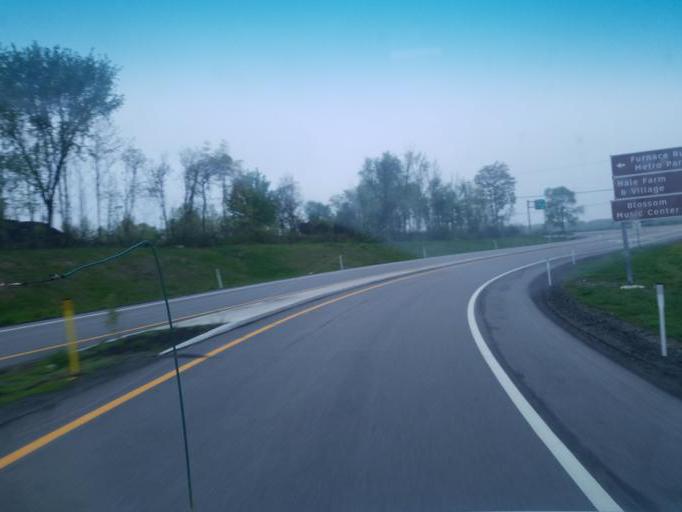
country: US
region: Ohio
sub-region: Summit County
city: Peninsula
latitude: 41.2444
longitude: -81.5924
